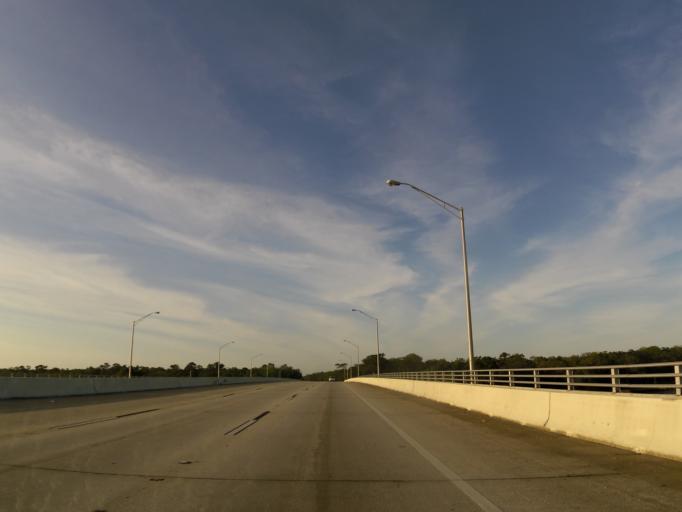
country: US
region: Florida
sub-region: Clay County
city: Orange Park
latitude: 30.1482
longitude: -81.7005
